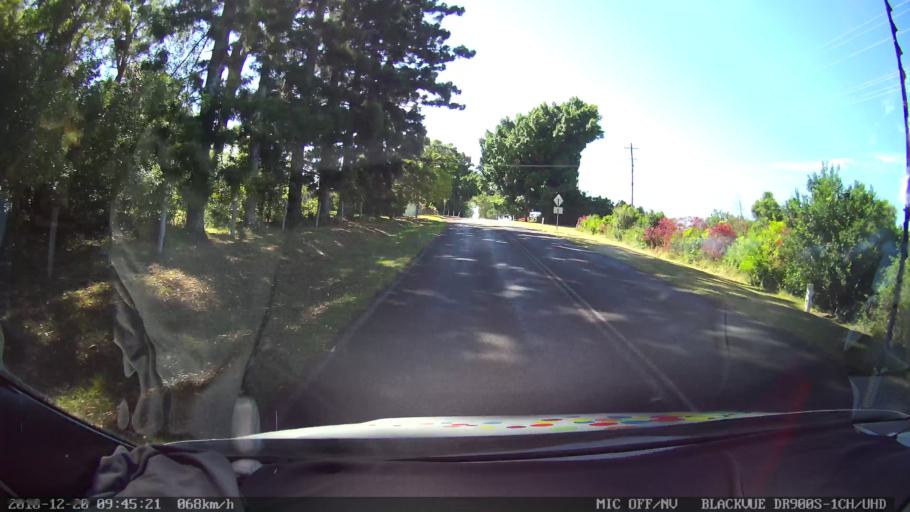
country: AU
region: New South Wales
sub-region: Lismore Municipality
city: Lismore
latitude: -28.7432
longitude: 153.2994
